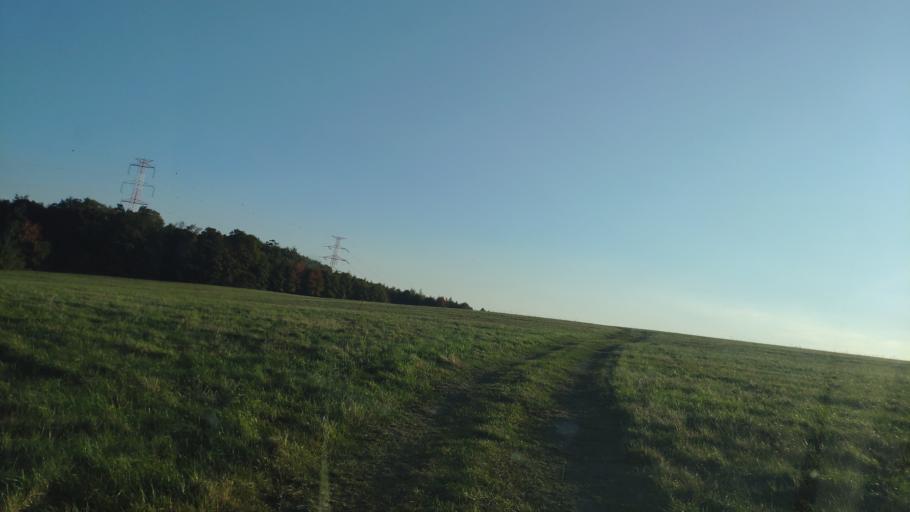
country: SK
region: Kosicky
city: Kosice
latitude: 48.7115
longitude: 21.1688
